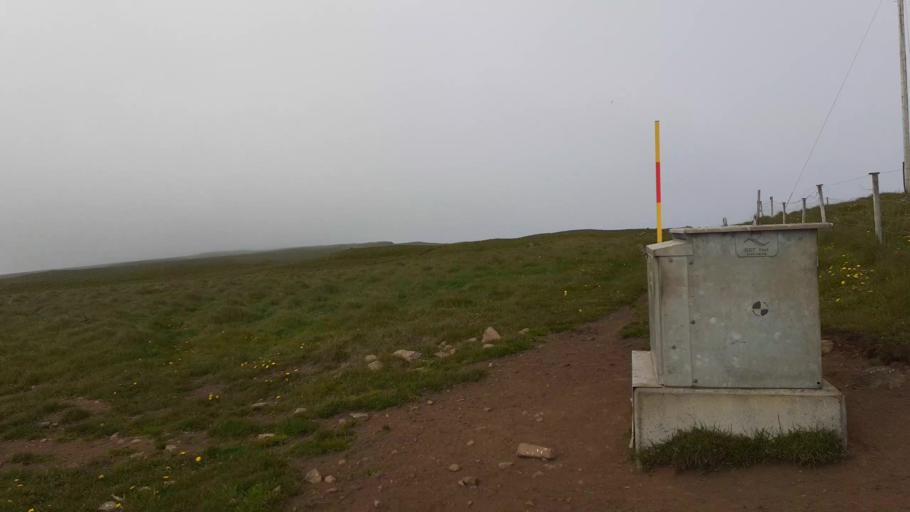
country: IS
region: Northeast
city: Dalvik
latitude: 66.5458
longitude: -17.9930
